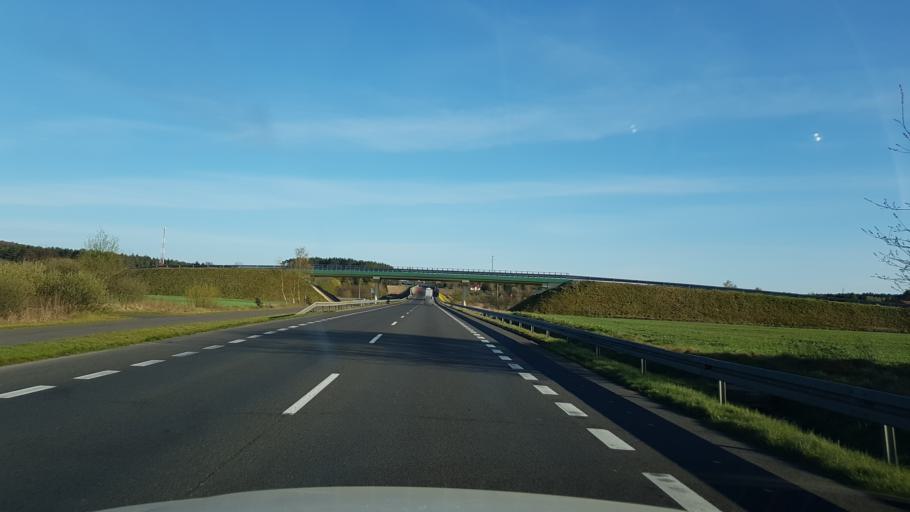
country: PL
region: West Pomeranian Voivodeship
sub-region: Powiat kamienski
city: Wolin
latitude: 53.8759
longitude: 14.5360
